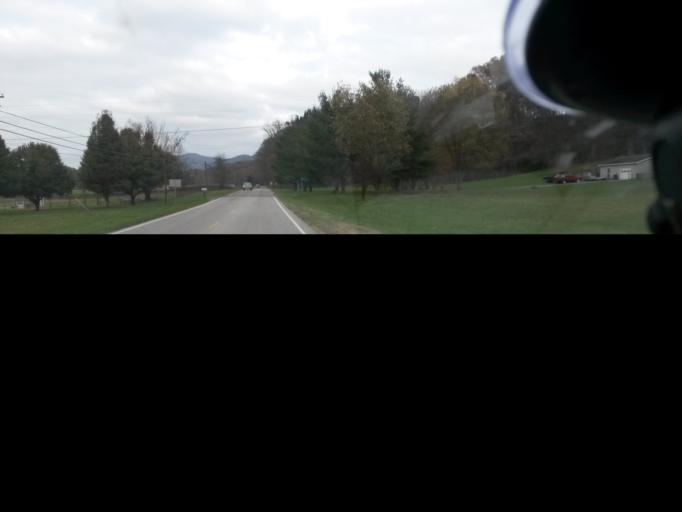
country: US
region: Virginia
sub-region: City of Buena Vista
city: Buena Vista
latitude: 37.7084
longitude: -79.3748
